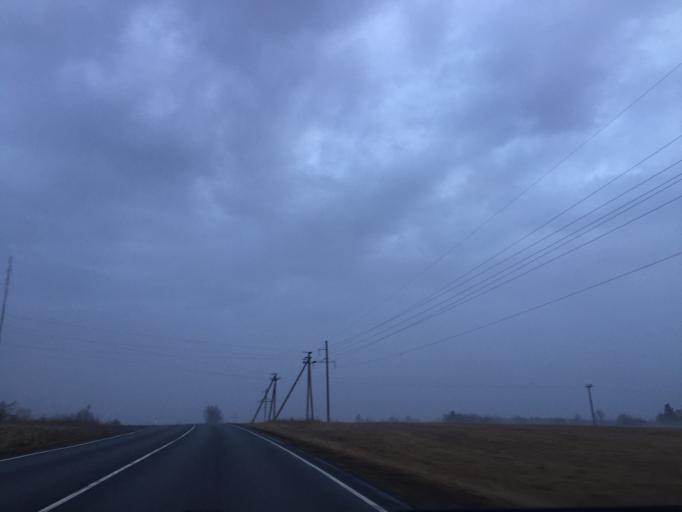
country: EE
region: Laeaene
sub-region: Lihula vald
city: Lihula
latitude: 58.6784
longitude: 23.8153
